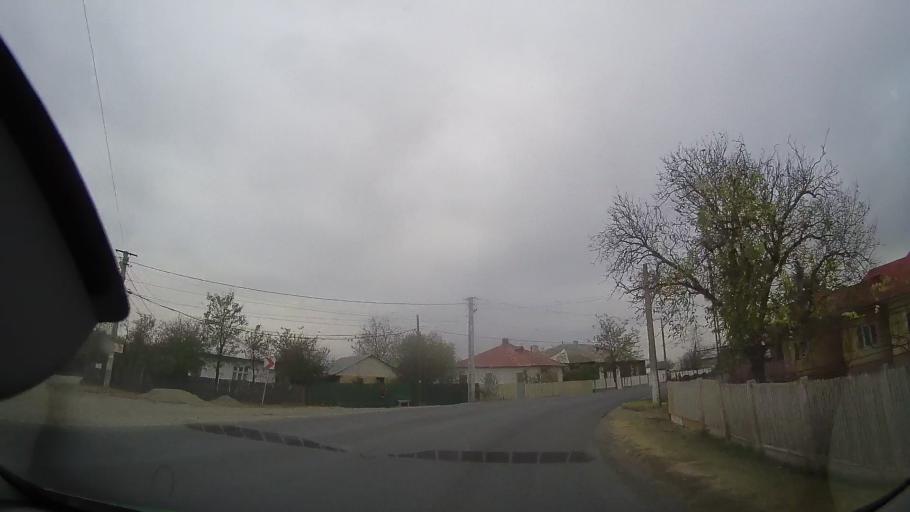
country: RO
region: Buzau
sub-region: Comuna Padina
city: Padina
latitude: 44.8245
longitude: 27.1111
